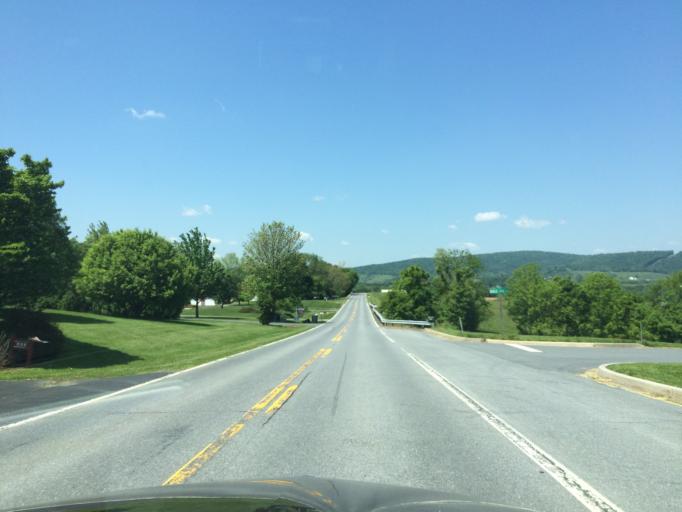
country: US
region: Maryland
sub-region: Frederick County
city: Myersville
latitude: 39.4828
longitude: -77.5492
